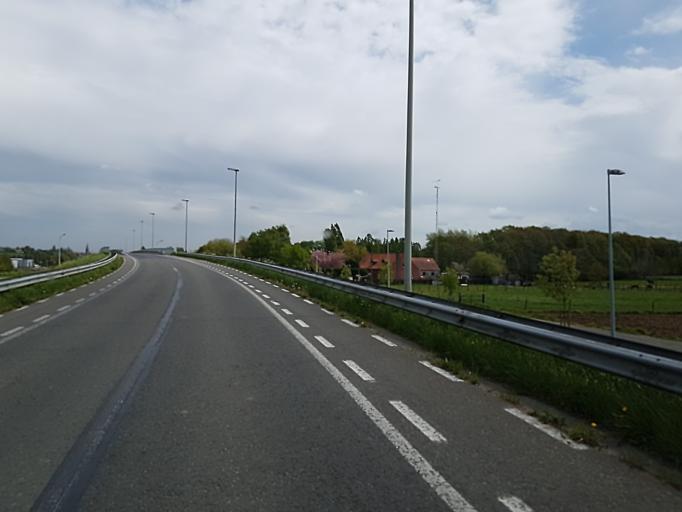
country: BE
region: Flanders
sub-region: Provincie West-Vlaanderen
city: Zonnebeke
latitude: 50.8369
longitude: 3.0030
